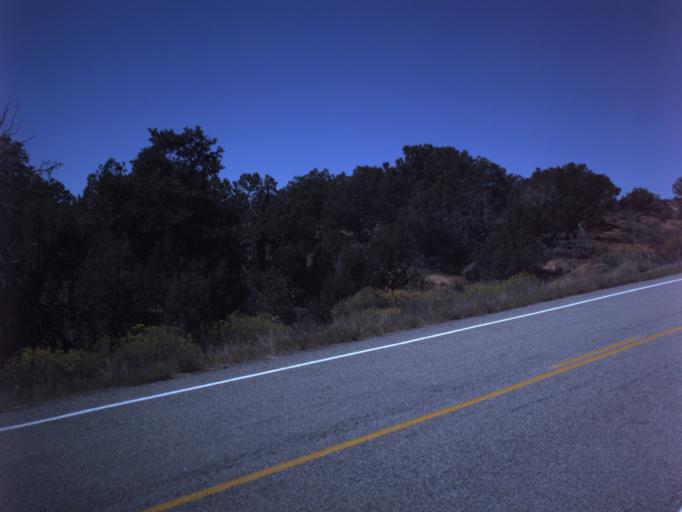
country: US
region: Utah
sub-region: San Juan County
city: Blanding
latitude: 37.5489
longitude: -109.7714
